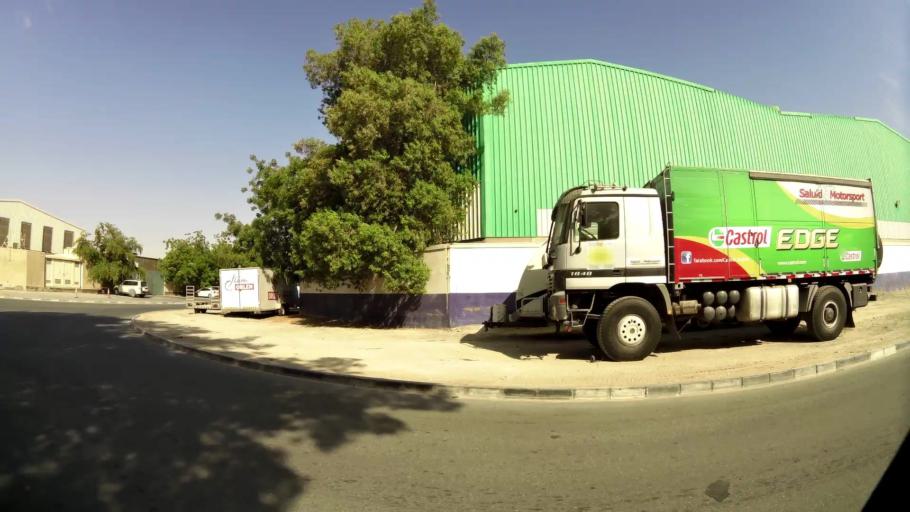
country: AE
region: Dubai
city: Dubai
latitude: 25.1228
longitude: 55.2102
